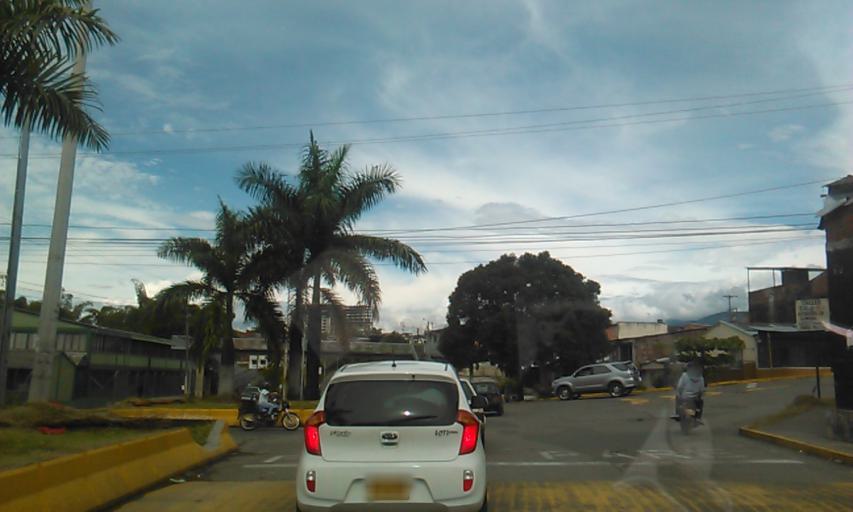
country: CO
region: Quindio
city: Armenia
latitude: 4.5295
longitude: -75.7071
